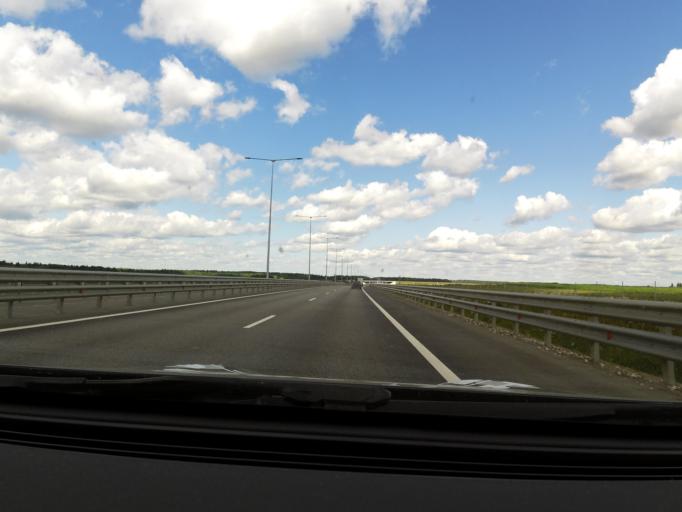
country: RU
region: Tverskaya
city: Vydropuzhsk
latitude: 57.2452
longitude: 34.8917
